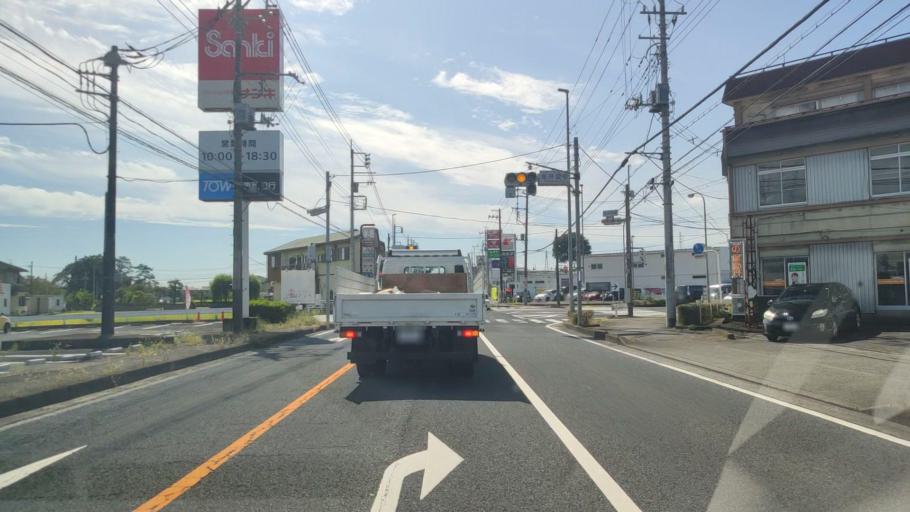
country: JP
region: Gunma
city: Shibukawa
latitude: 36.5103
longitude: 139.0053
